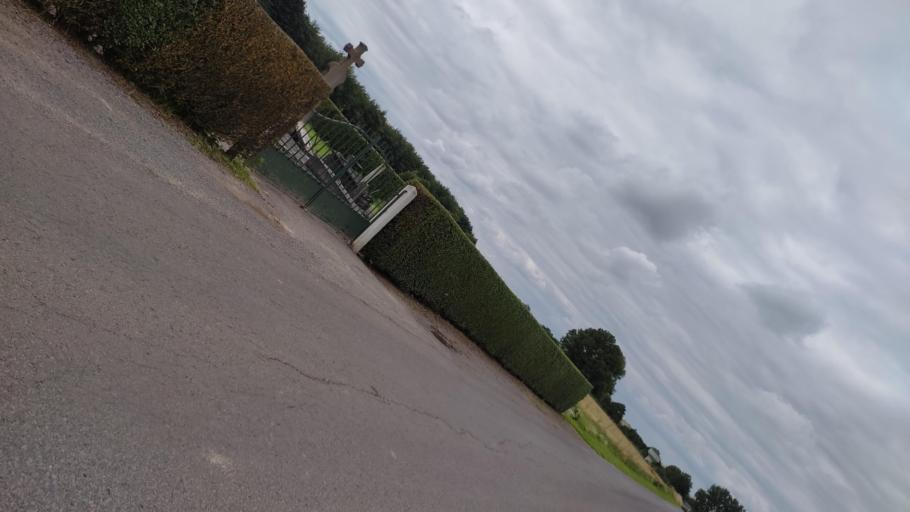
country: FR
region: Nord-Pas-de-Calais
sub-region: Departement du Pas-de-Calais
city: Beaumetz-les-Loges
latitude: 50.2345
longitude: 2.6308
